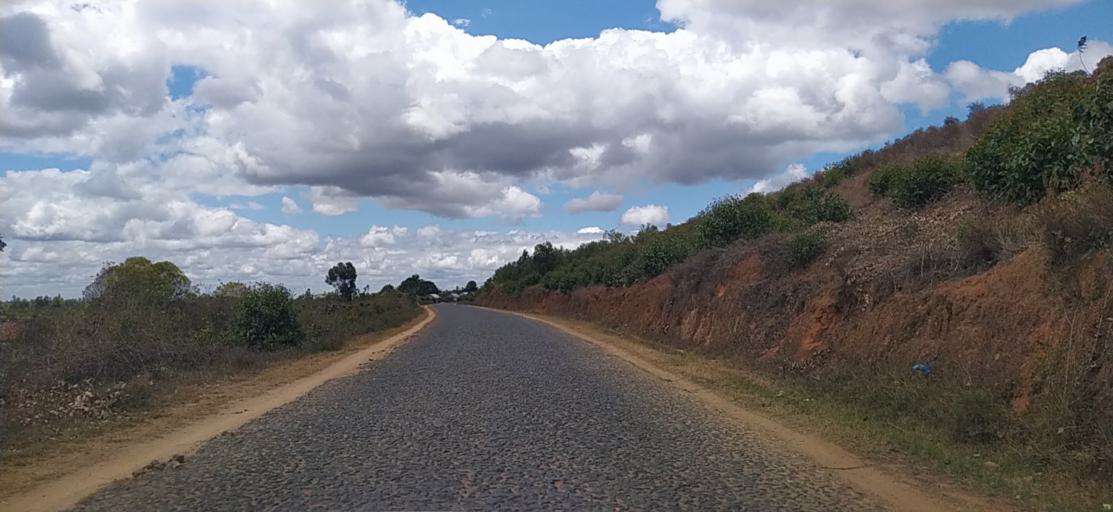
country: MG
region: Alaotra Mangoro
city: Moramanga
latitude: -18.7558
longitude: 48.2592
